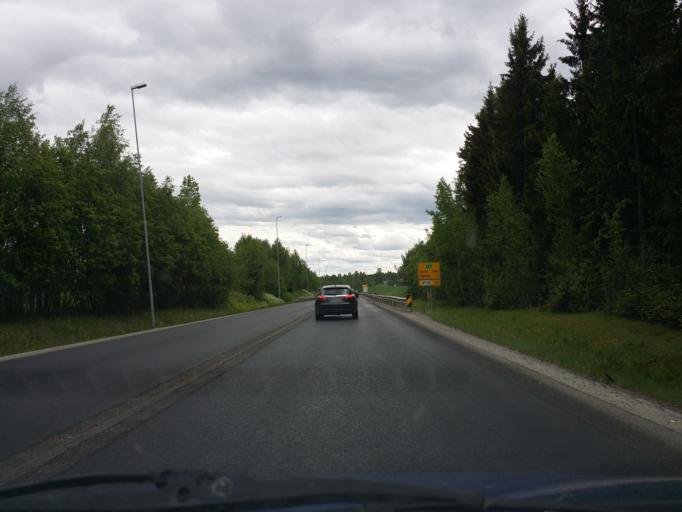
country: NO
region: Hedmark
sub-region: Hamar
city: Hamar
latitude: 60.8379
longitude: 11.0700
